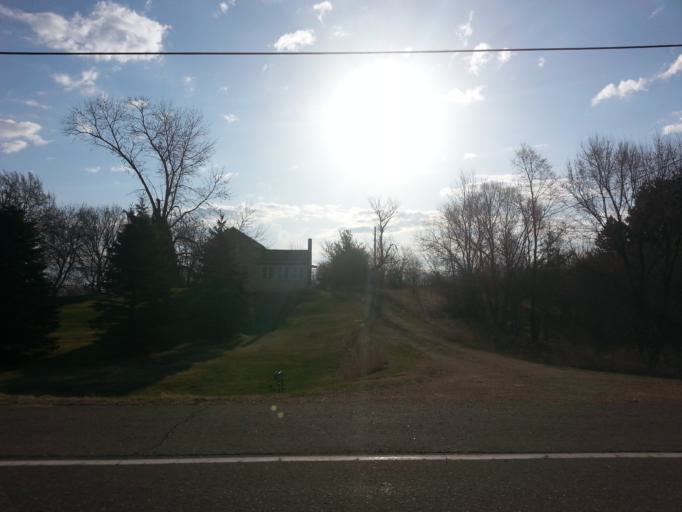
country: US
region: Minnesota
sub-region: Washington County
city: Afton
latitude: 44.9309
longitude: -92.8428
